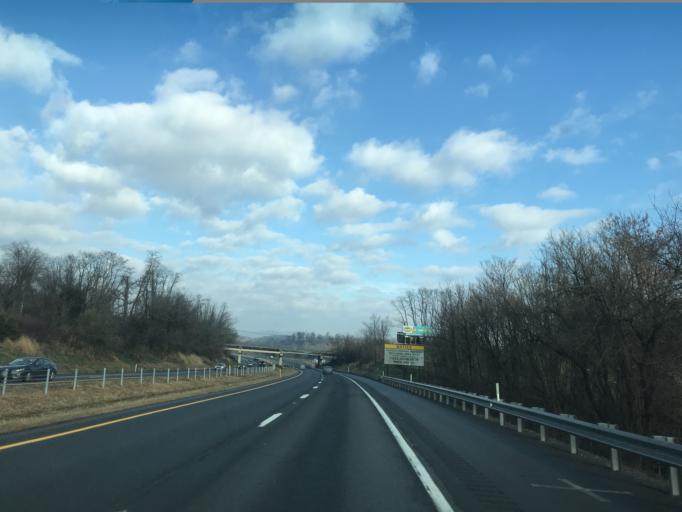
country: US
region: Maryland
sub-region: Washington County
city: Hancock
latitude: 39.7467
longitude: -78.1814
